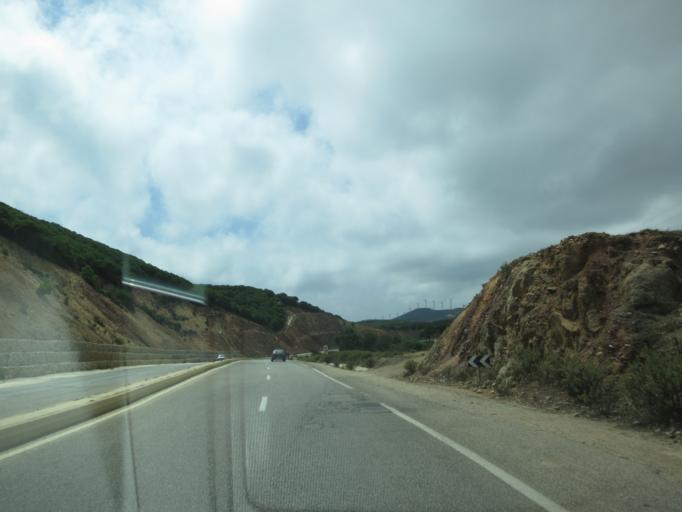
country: ES
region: Ceuta
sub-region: Ceuta
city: Ceuta
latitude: 35.8655
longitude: -5.4097
